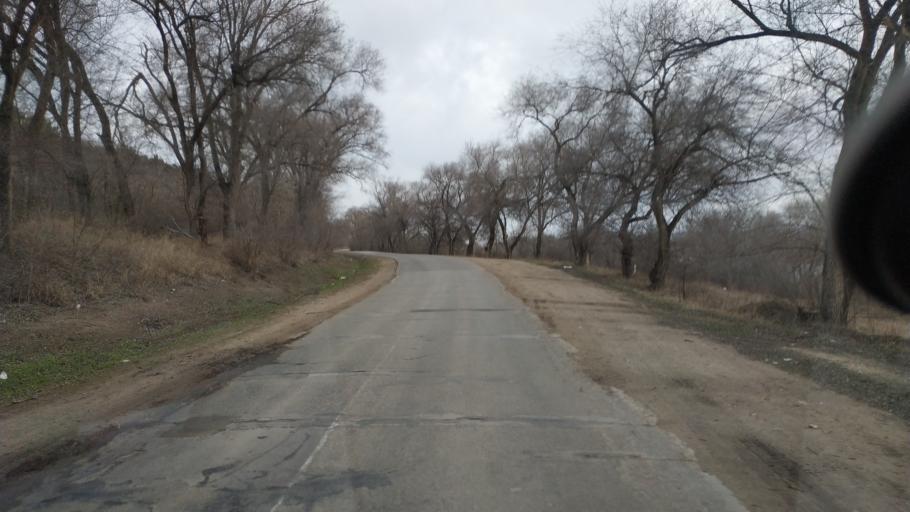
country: MD
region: Criuleni
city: Criuleni
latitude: 47.2263
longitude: 29.1616
